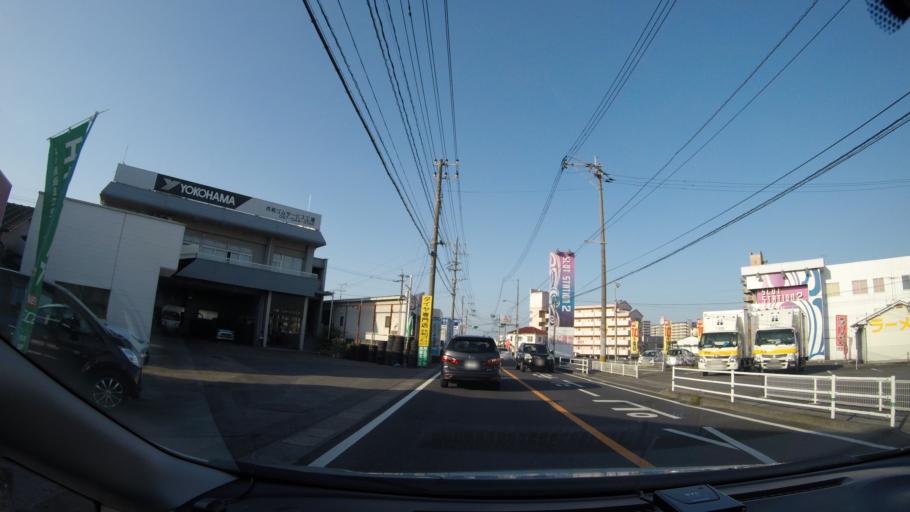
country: JP
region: Oita
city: Oita
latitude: 33.2102
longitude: 131.6065
